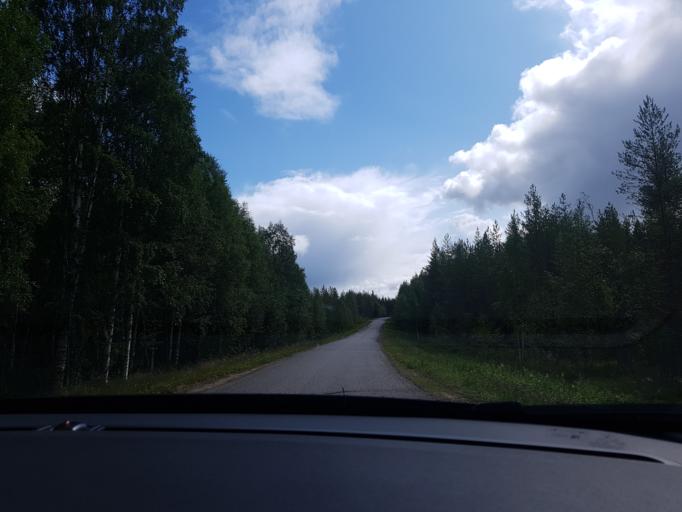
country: FI
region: Kainuu
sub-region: Kehys-Kainuu
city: Kuhmo
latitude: 64.4499
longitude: 29.6853
